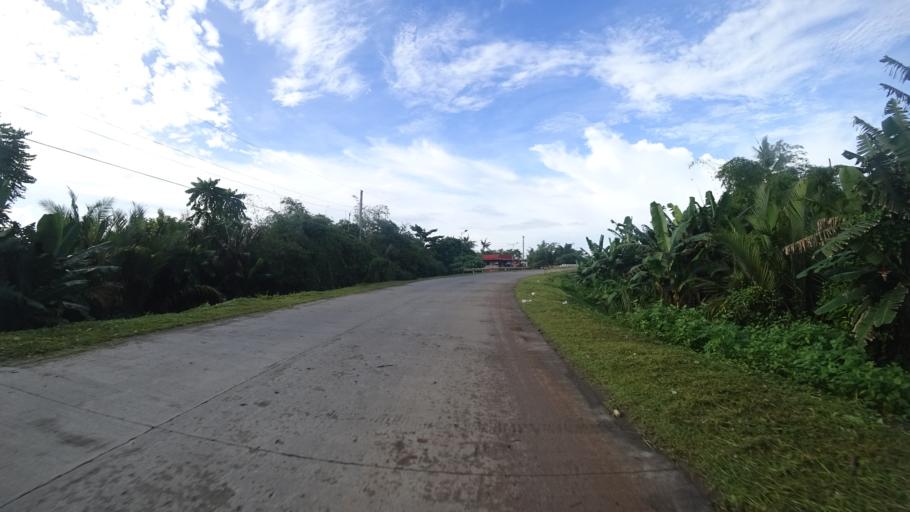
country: PH
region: Eastern Visayas
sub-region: Province of Leyte
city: Palo
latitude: 11.1610
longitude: 125.0032
